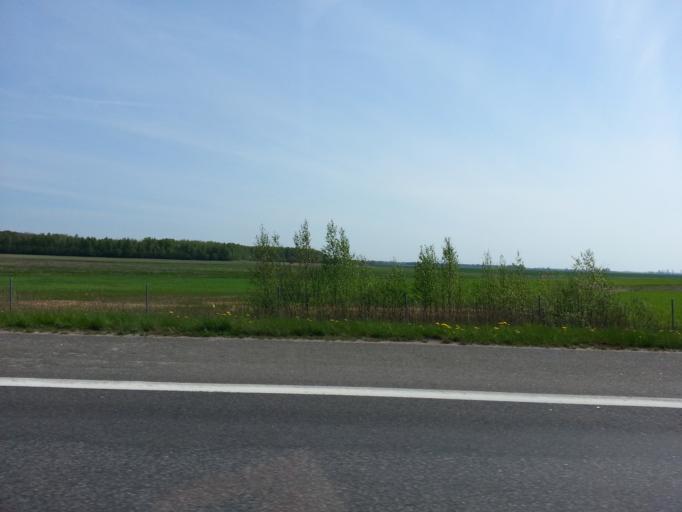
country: LT
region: Vilnius County
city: Ukmerge
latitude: 55.4121
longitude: 24.6953
